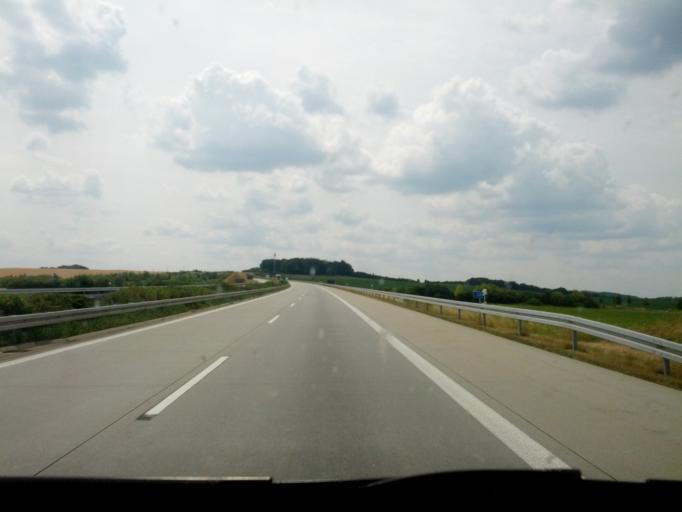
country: DE
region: Saxony
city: Liebstadt
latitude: 50.8899
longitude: 13.8829
